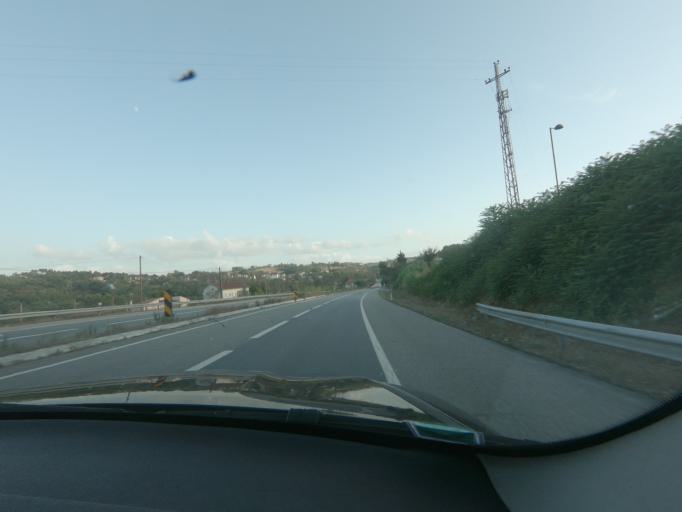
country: PT
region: Viseu
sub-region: Santa Comba Dao
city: Santa Comba Dao
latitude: 40.3976
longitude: -8.1264
